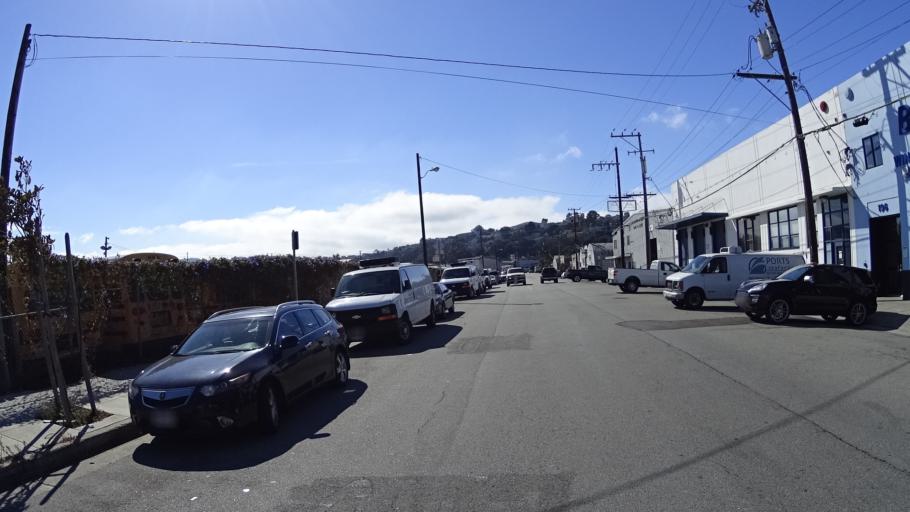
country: US
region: California
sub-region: San Francisco County
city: San Francisco
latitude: 37.7469
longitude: -122.3992
